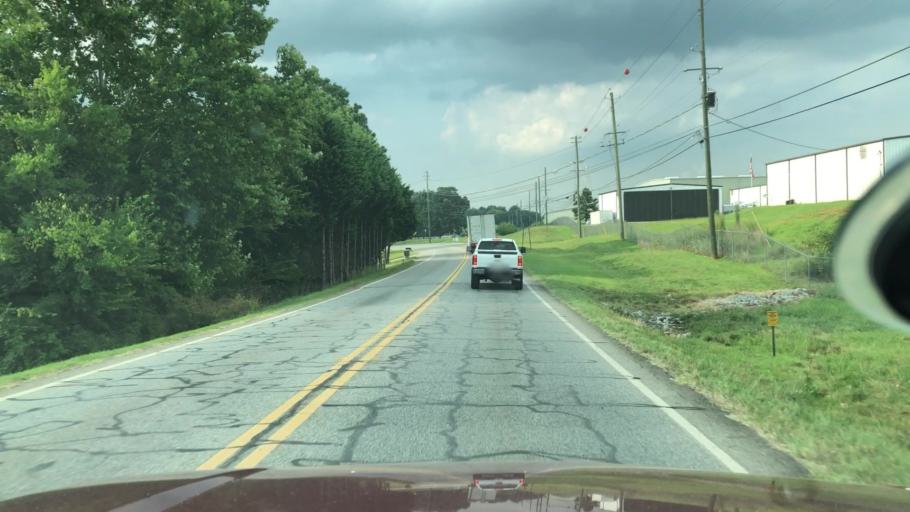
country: US
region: Georgia
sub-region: Bartow County
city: Cartersville
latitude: 34.1253
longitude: -84.8505
